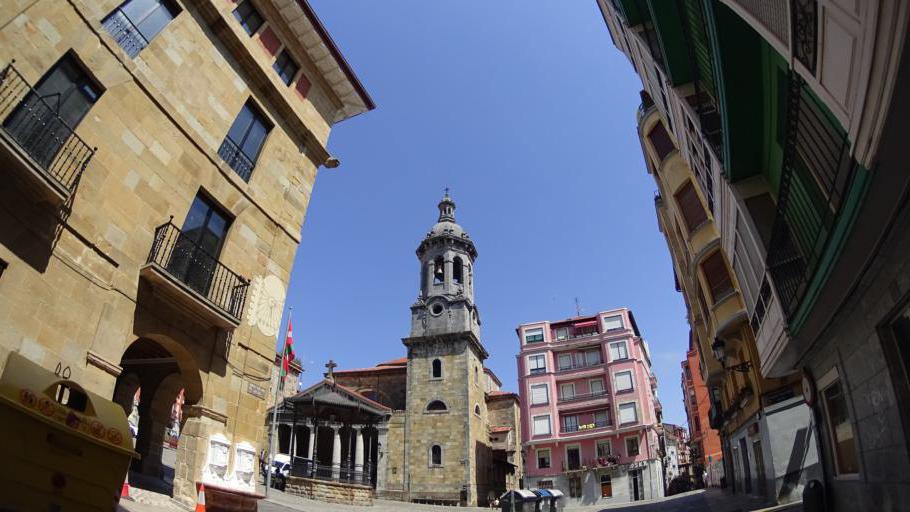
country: ES
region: Basque Country
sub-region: Bizkaia
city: Bermeo
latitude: 43.4202
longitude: -2.7229
